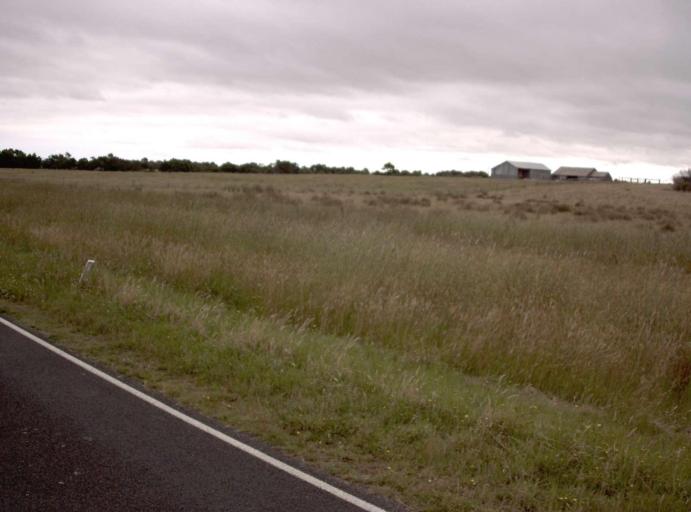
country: AU
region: Victoria
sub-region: Wellington
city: Sale
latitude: -38.5529
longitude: 146.8837
